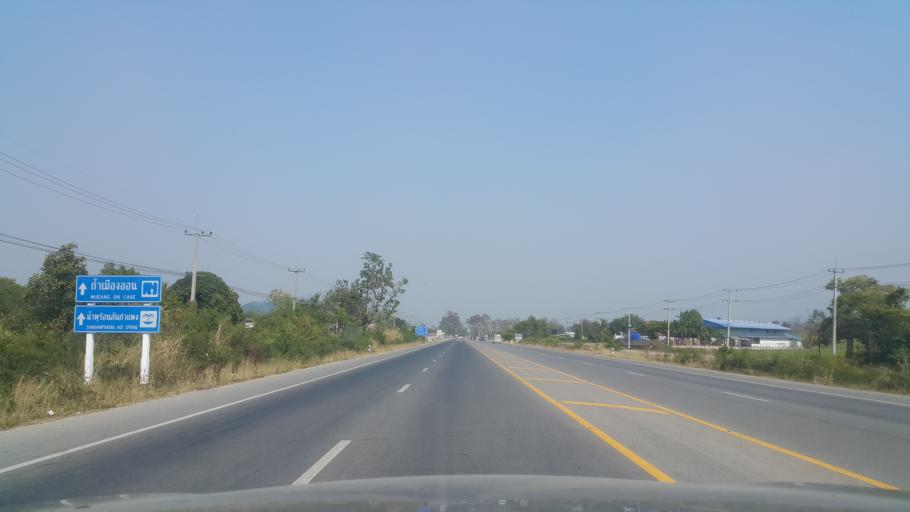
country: TH
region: Chiang Mai
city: San Kamphaeng
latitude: 18.7225
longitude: 99.1602
